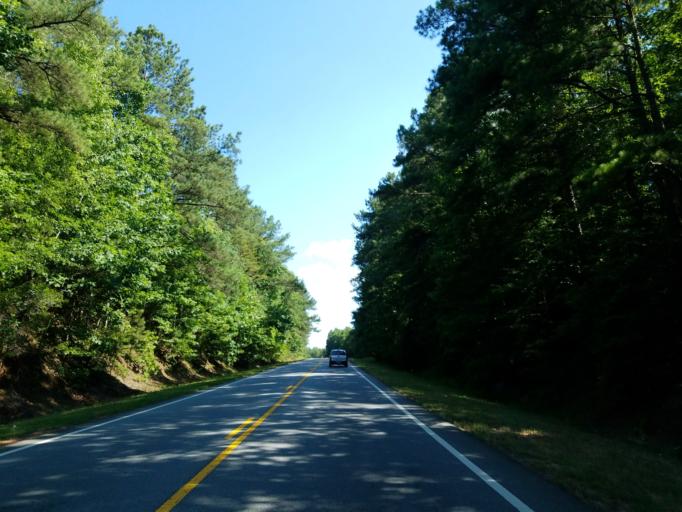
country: US
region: Georgia
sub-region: Crawford County
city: Roberta
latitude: 32.7678
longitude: -84.0214
